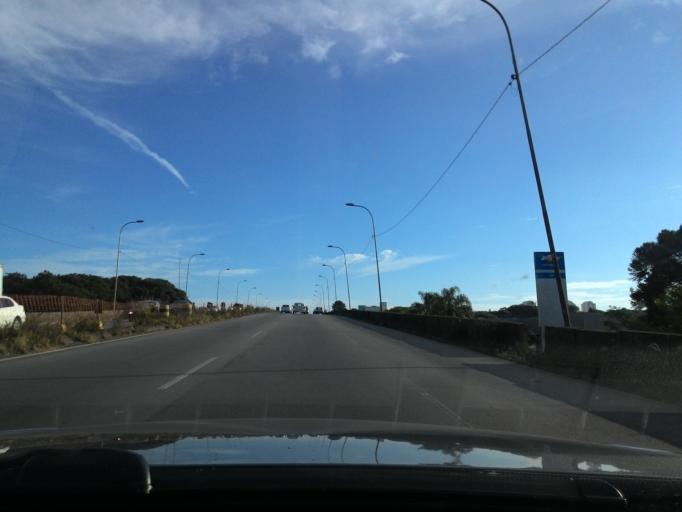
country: BR
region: Parana
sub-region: Pinhais
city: Pinhais
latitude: -25.4263
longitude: -49.2276
